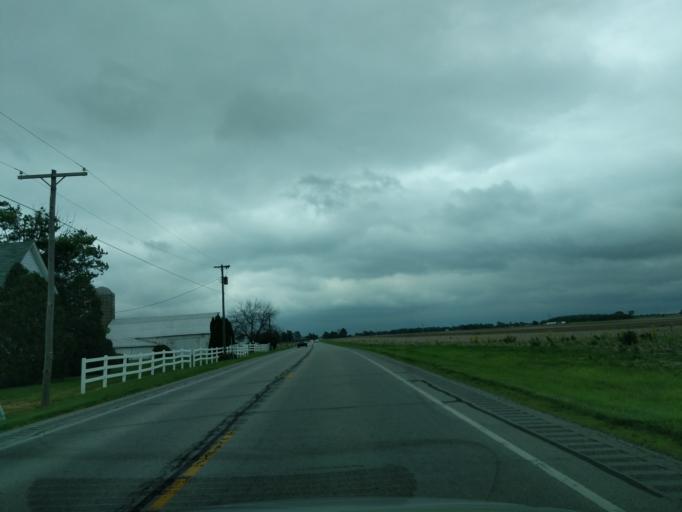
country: US
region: Indiana
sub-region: Madison County
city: Frankton
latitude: 40.2775
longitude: -85.7849
